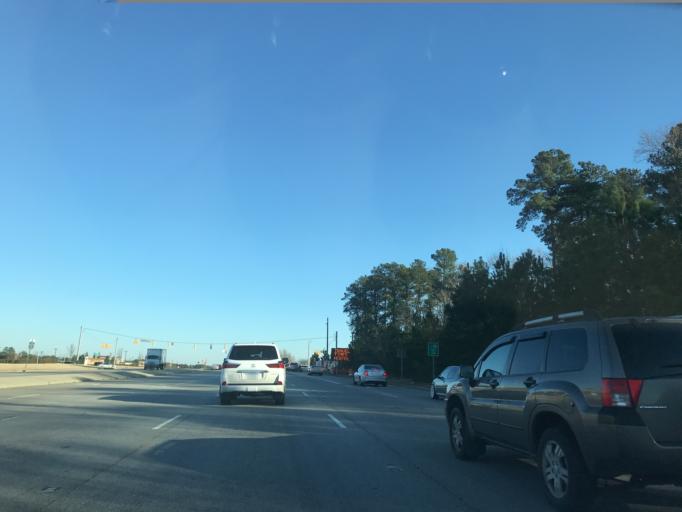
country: US
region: North Carolina
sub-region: Wake County
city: Garner
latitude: 35.6968
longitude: -78.5865
